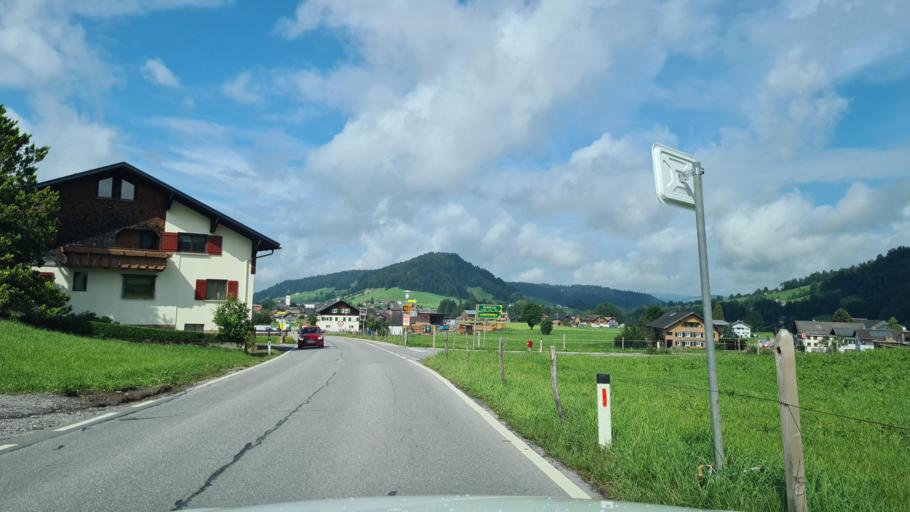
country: AT
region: Vorarlberg
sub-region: Politischer Bezirk Bregenz
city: Riefensberg
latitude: 47.4568
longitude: 9.9790
